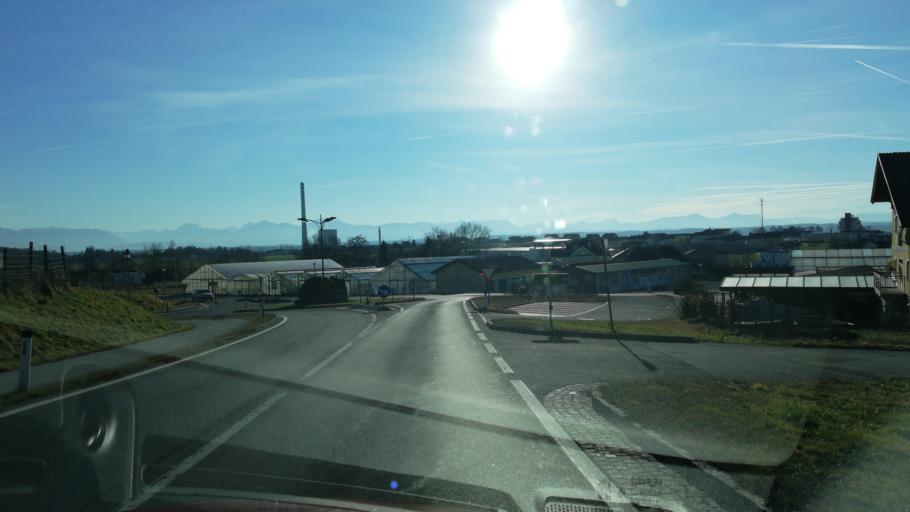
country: DE
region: Bavaria
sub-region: Upper Bavaria
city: Fridolfing
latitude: 48.0467
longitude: 12.8441
